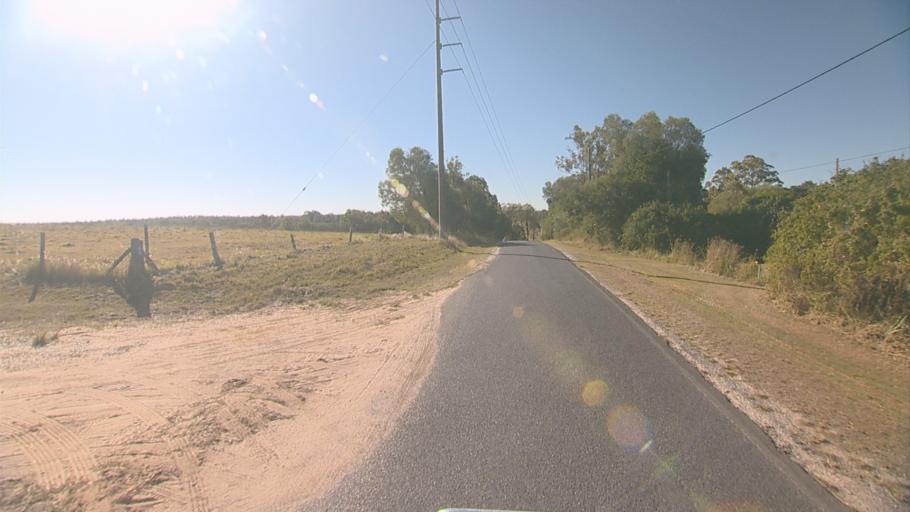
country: AU
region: Queensland
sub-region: Logan
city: Chambers Flat
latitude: -27.7704
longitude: 153.0599
